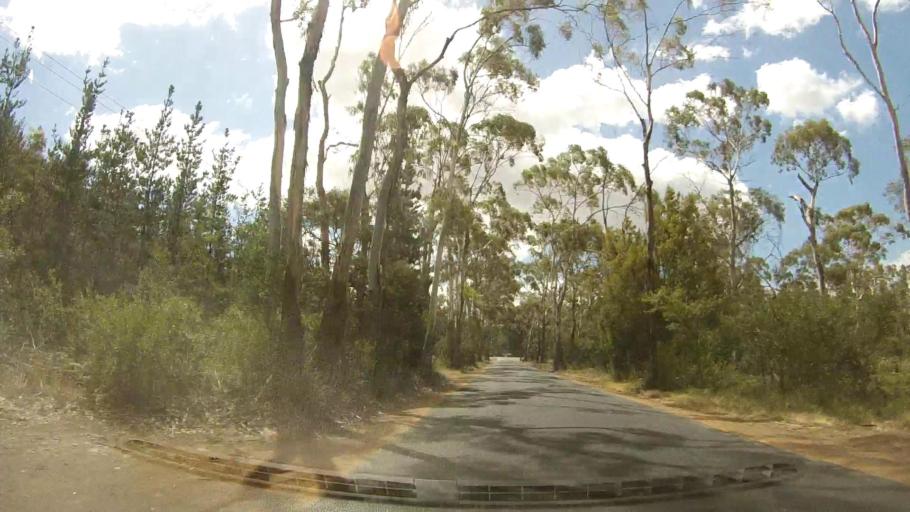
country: AU
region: Tasmania
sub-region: Clarence
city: Seven Mile Beach
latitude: -42.8234
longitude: 147.5054
